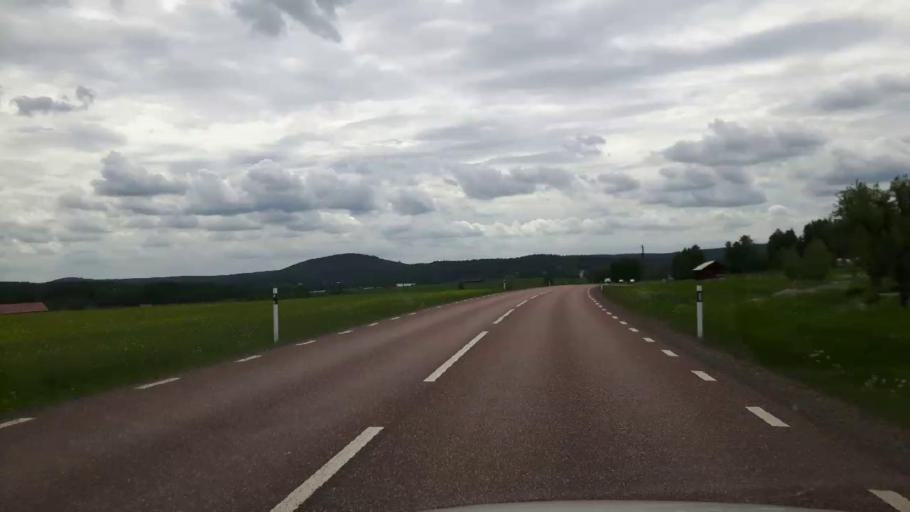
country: SE
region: Dalarna
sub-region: Hedemora Kommun
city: Brunna
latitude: 60.2460
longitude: 16.0098
